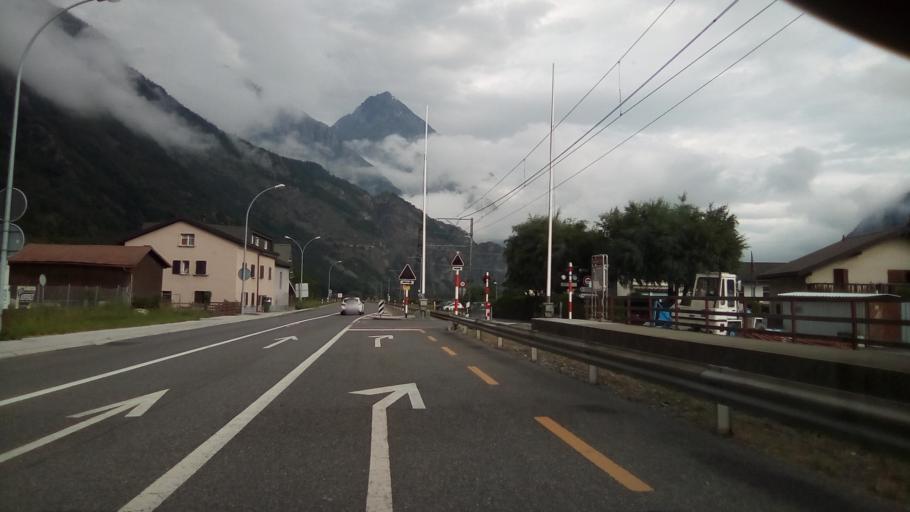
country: CH
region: Valais
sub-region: Martigny District
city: Martigny-Ville
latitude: 46.1099
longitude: 7.0647
